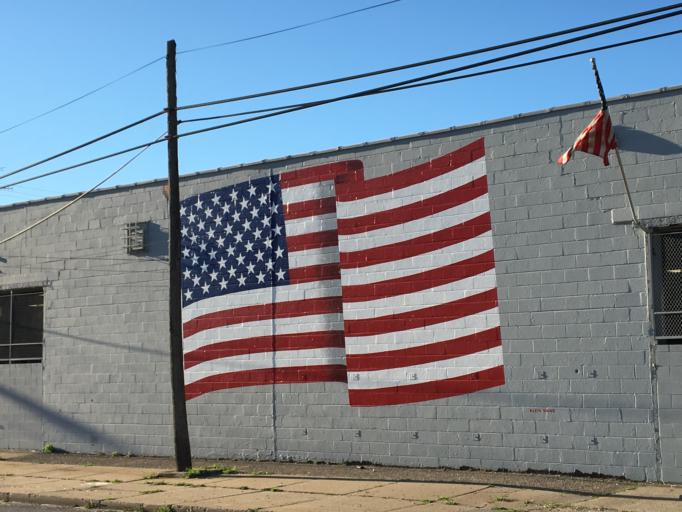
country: US
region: Michigan
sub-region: Wayne County
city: Hamtramck
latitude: 42.4051
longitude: -83.0198
